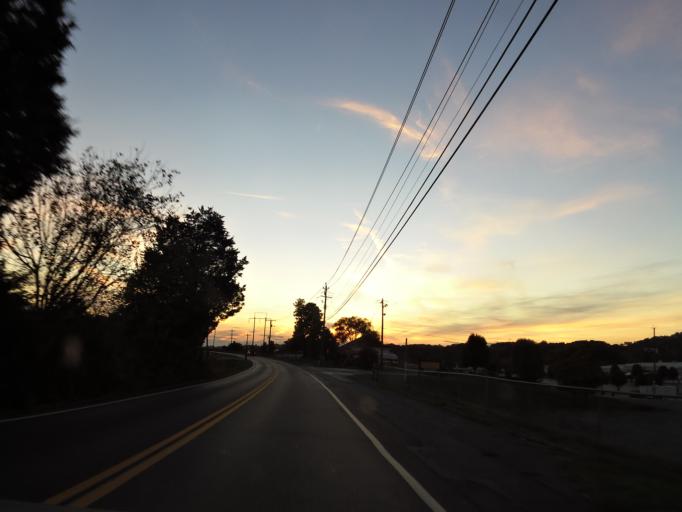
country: US
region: Tennessee
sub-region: Sevier County
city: Sevierville
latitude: 35.9792
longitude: -83.6168
